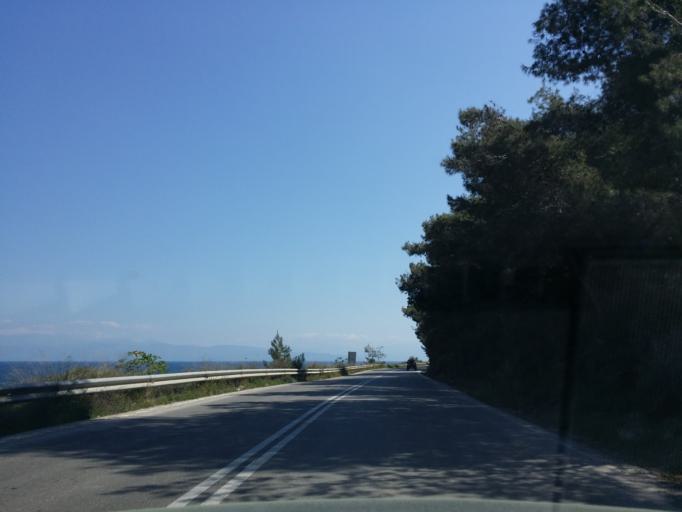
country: GR
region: West Greece
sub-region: Nomos Achaias
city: Akrata
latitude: 38.1731
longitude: 22.2851
